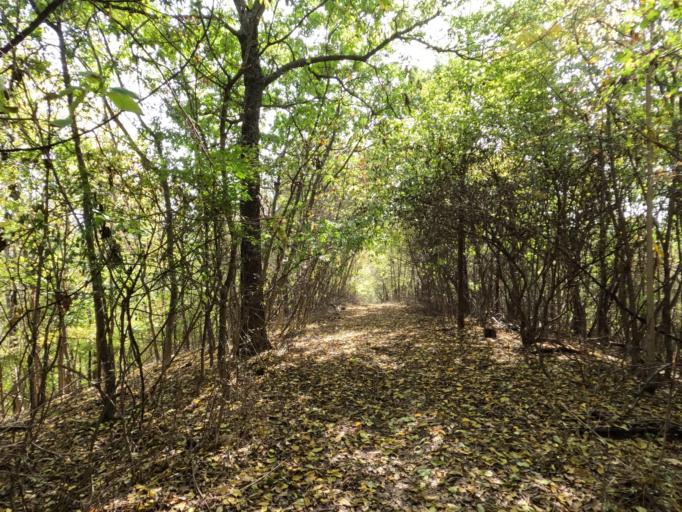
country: HU
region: Tolna
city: Szentgalpuszta
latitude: 46.3447
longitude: 18.6288
